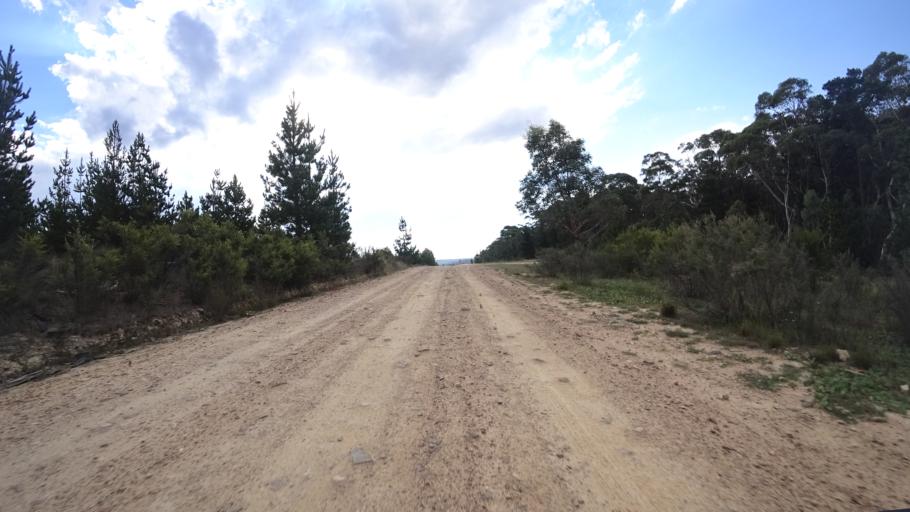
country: AU
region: New South Wales
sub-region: Lithgow
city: Lithgow
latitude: -33.3505
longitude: 150.2587
